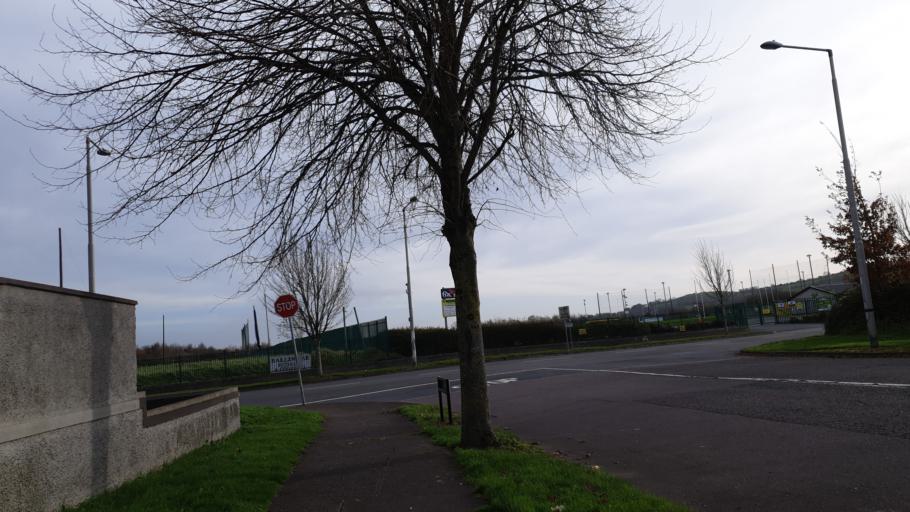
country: IE
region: Munster
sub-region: County Cork
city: Passage West
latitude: 51.8905
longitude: -8.3955
